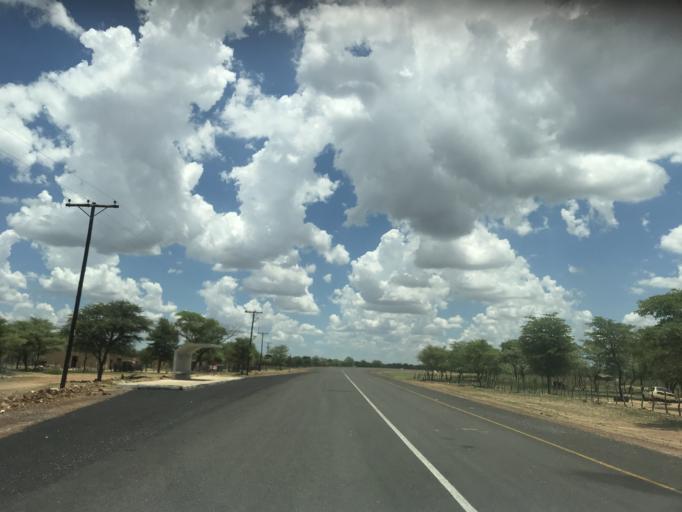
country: BW
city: Mabuli
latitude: -25.8044
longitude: 24.8154
